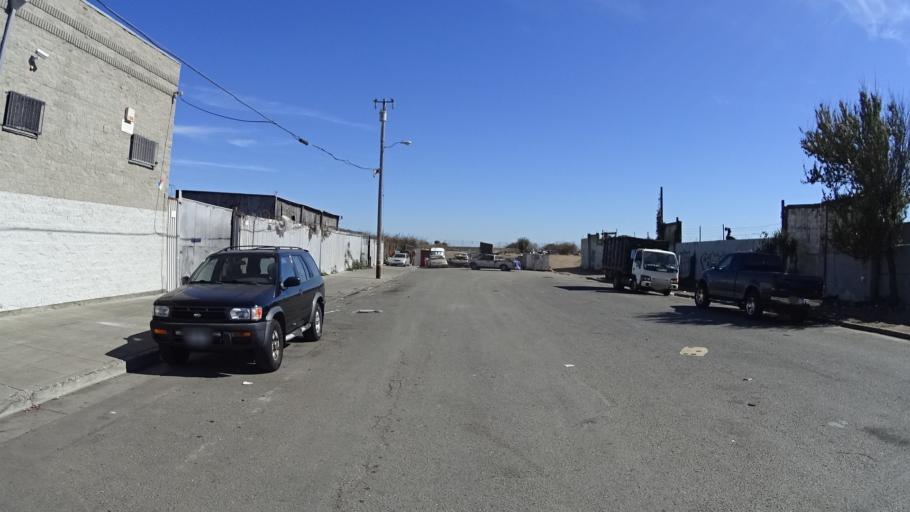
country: US
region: California
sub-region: San Mateo County
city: Brisbane
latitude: 37.7253
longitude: -122.3855
